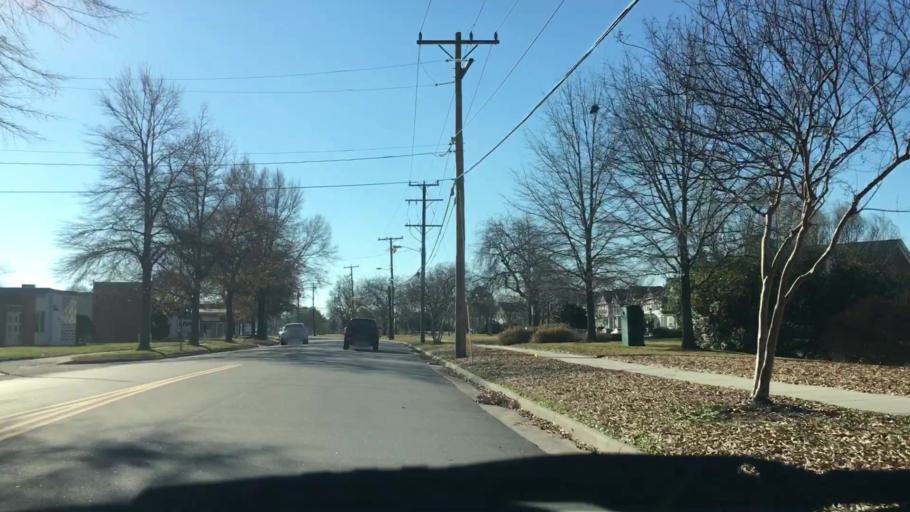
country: US
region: Virginia
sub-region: City of Norfolk
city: Norfolk
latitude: 36.8568
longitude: -76.2490
